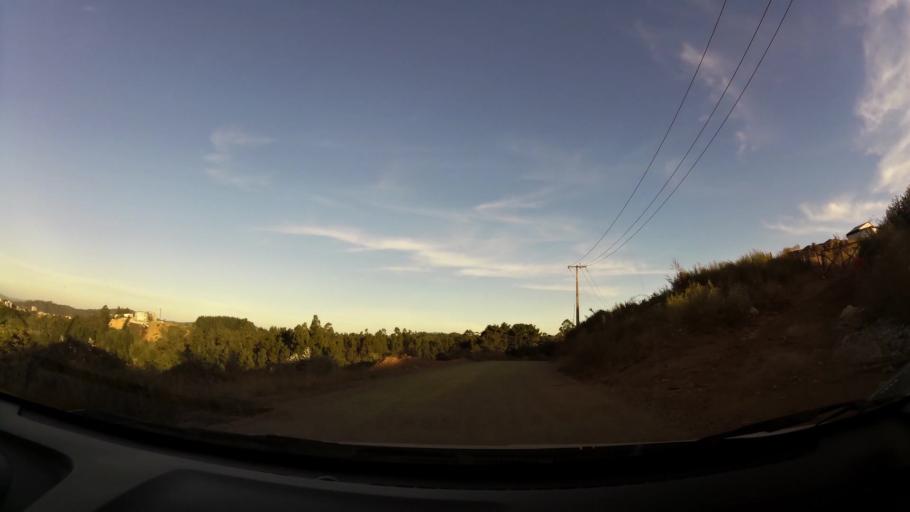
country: CL
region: Biobio
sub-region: Provincia de Concepcion
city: Concepcion
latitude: -36.8540
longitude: -73.0904
